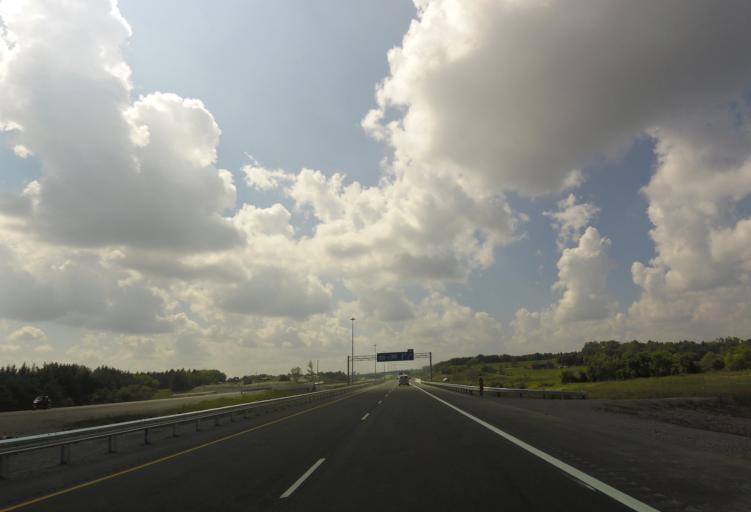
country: CA
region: Ontario
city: Ajax
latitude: 43.9517
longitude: -78.9880
